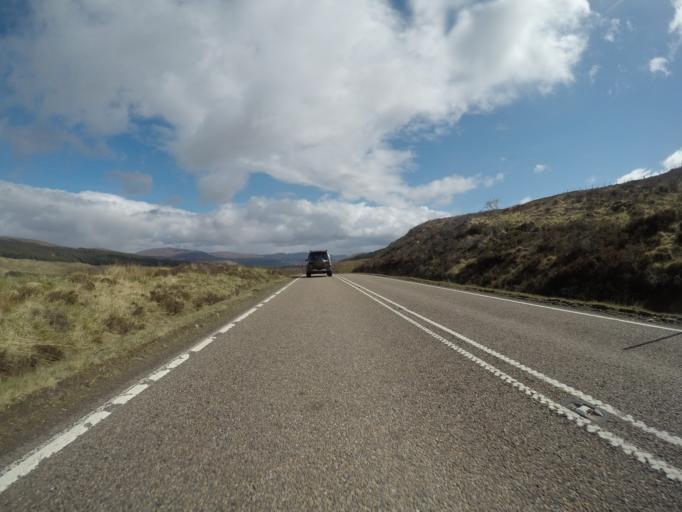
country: GB
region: Scotland
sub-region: Highland
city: Spean Bridge
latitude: 57.1212
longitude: -4.9739
